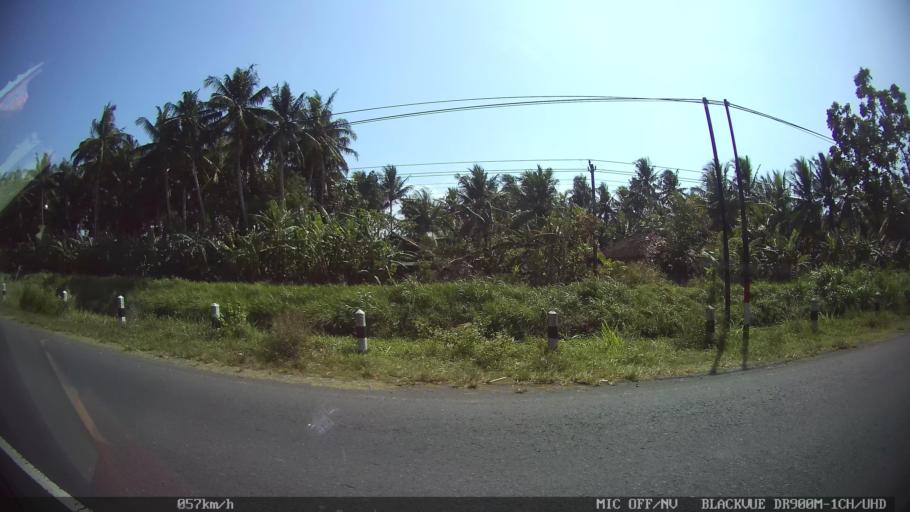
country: ID
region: Daerah Istimewa Yogyakarta
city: Srandakan
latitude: -7.9395
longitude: 110.1595
